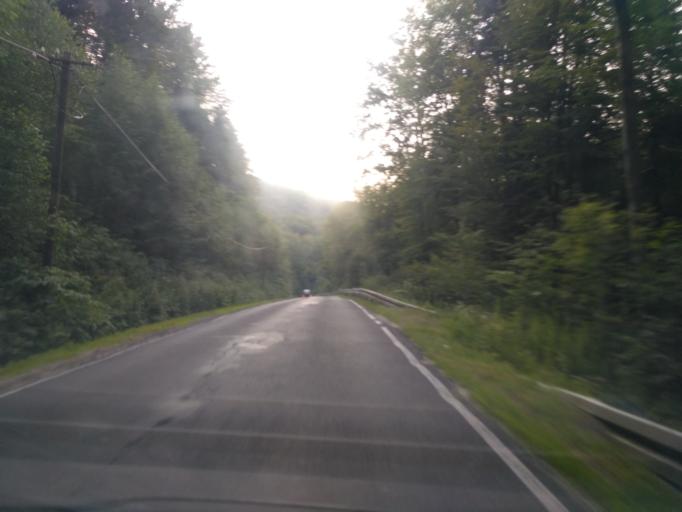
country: PL
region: Subcarpathian Voivodeship
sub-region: Powiat krosnienski
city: Korczyna
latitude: 49.7549
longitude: 21.7972
